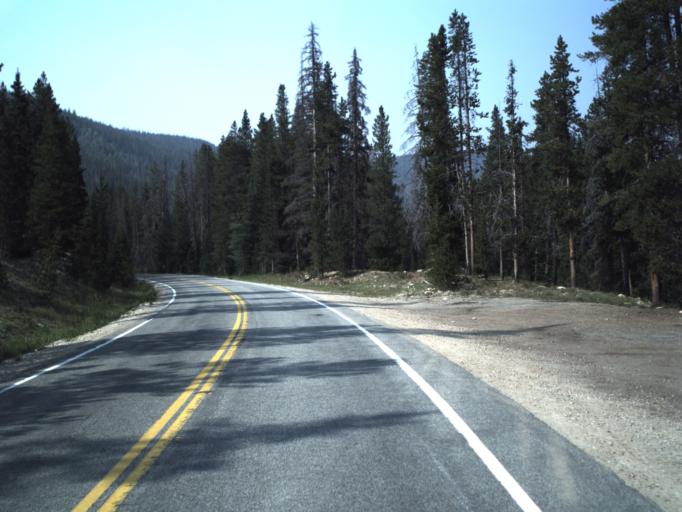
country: US
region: Utah
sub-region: Summit County
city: Francis
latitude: 40.6117
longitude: -110.9618
